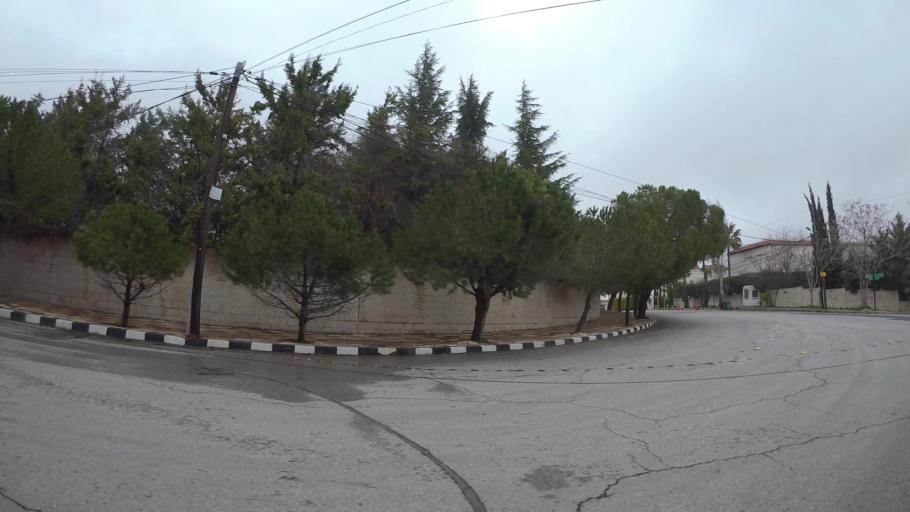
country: JO
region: Amman
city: Al Bunayyat ash Shamaliyah
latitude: 31.9367
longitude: 35.8814
